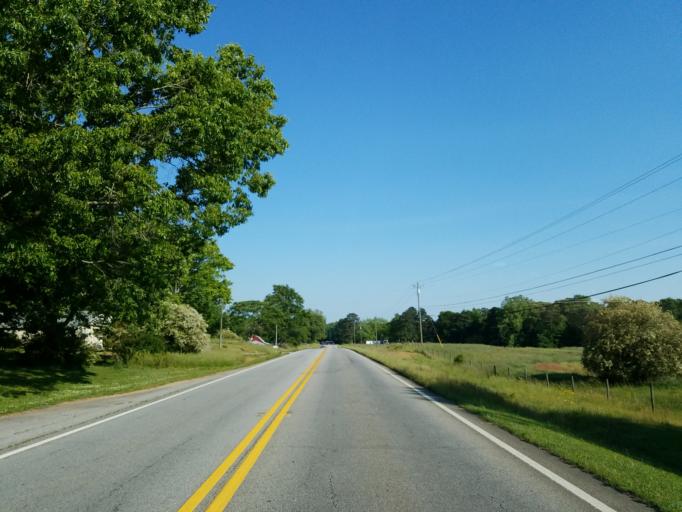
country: US
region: Georgia
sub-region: Carroll County
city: Villa Rica
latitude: 33.7711
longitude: -84.9592
